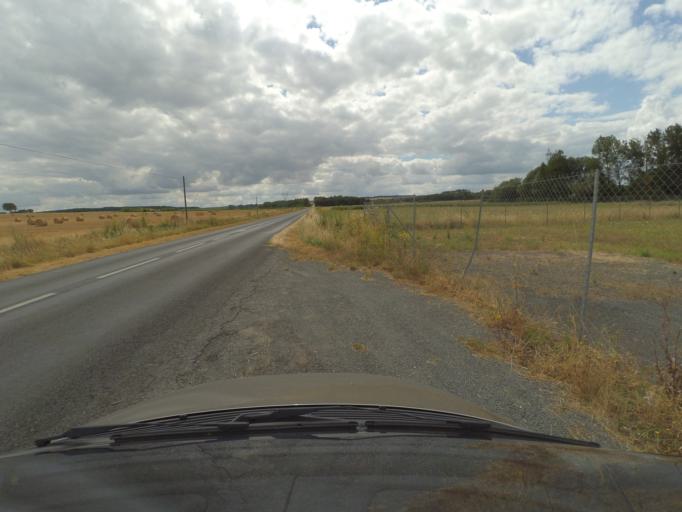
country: FR
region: Poitou-Charentes
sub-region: Departement de la Vienne
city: Saint-Gervais-les-Trois-Clochers
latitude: 46.9422
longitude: 0.4198
